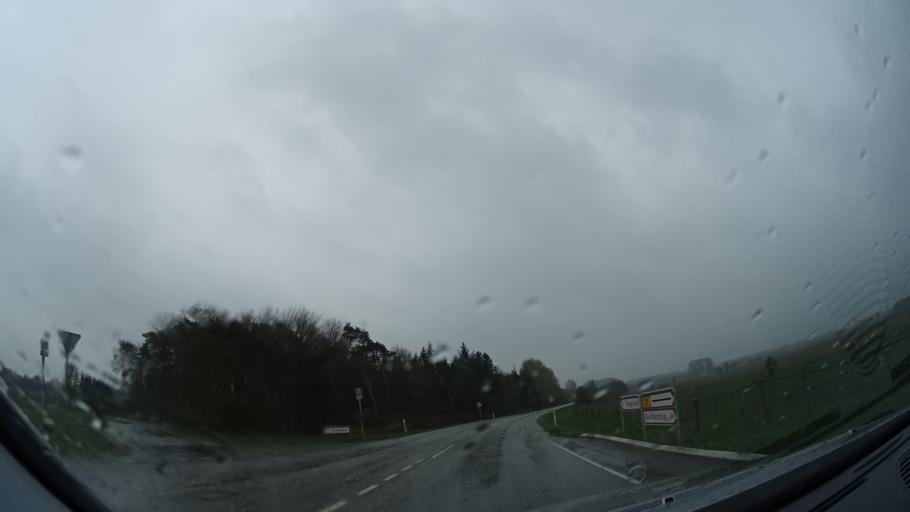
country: DK
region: Zealand
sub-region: Holbaek Kommune
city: Holbaek
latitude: 55.7651
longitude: 11.6304
